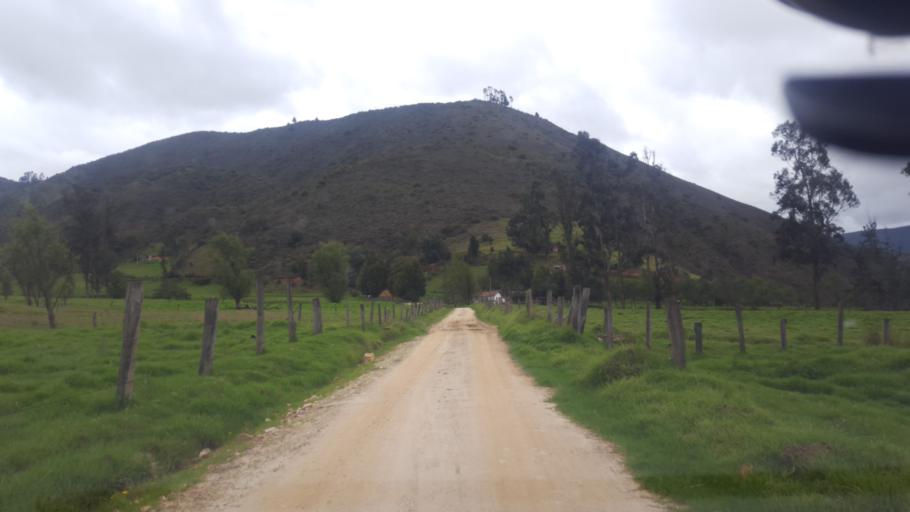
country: CO
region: Boyaca
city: Belen
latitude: 6.0135
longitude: -72.8612
